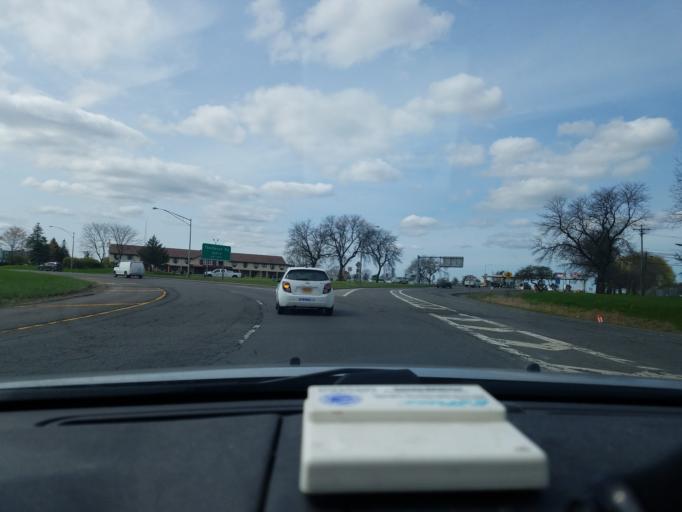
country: US
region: New York
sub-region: Onondaga County
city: East Syracuse
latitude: 43.0881
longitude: -76.0892
